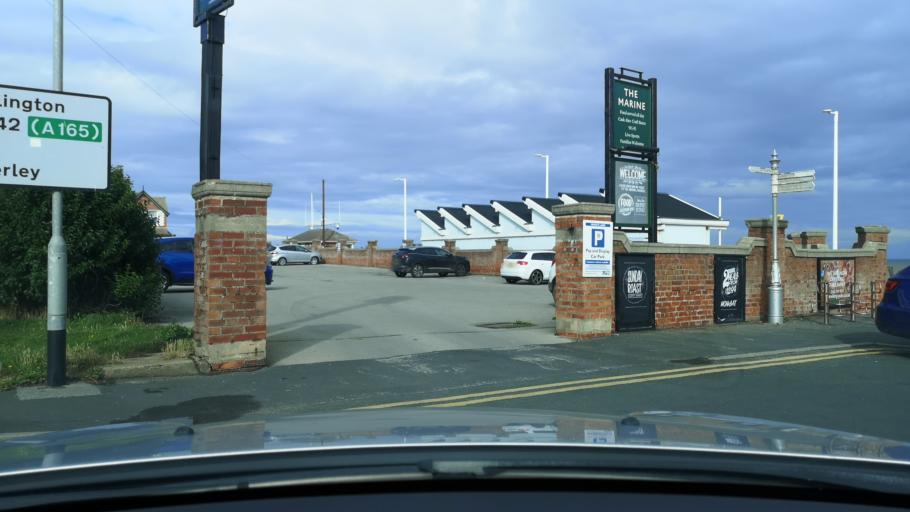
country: GB
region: England
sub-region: East Riding of Yorkshire
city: Hornsea
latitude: 53.9156
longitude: -0.1618
